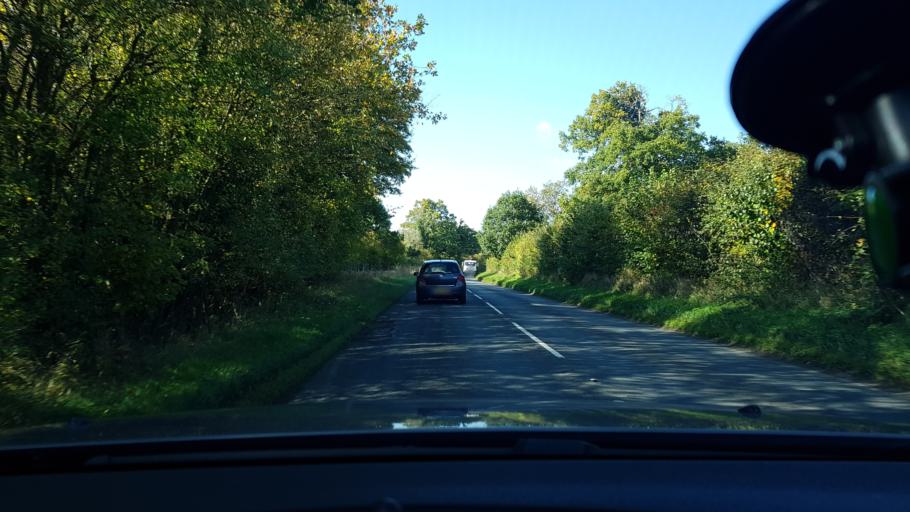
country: GB
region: England
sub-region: Wiltshire
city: Chilton Foliat
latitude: 51.4368
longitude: -1.5655
